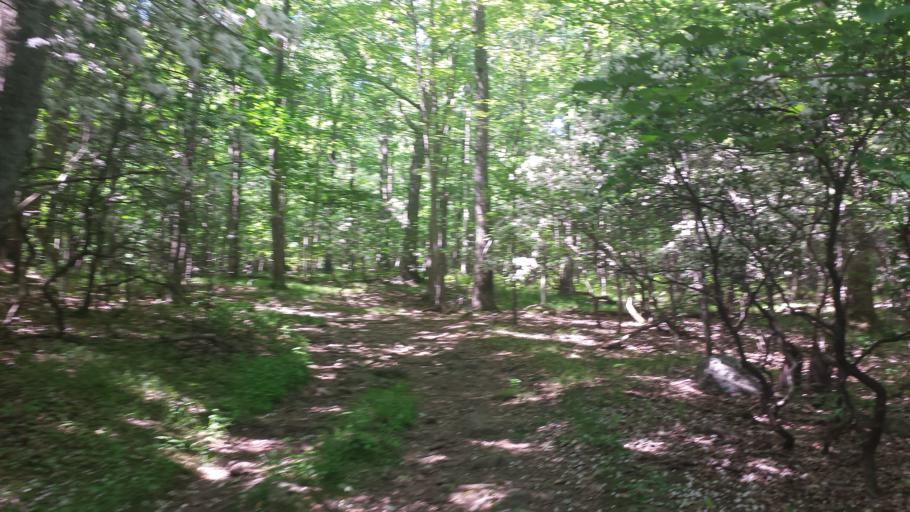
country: US
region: New York
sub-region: Westchester County
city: Pound Ridge
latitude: 41.2335
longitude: -73.5941
